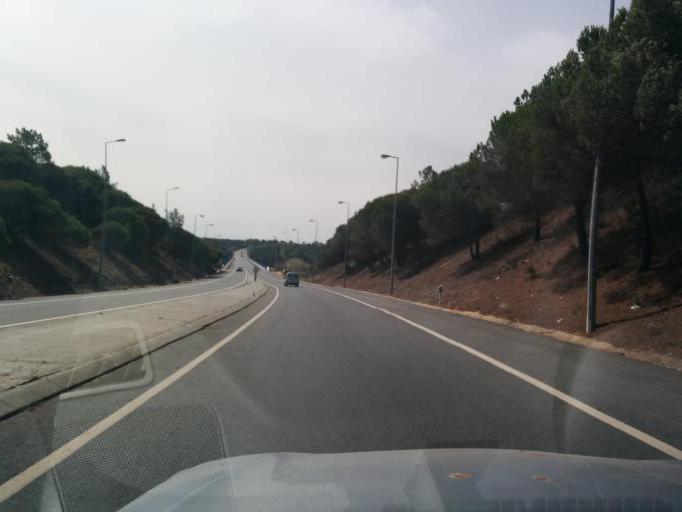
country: PT
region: Beja
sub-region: Odemira
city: Vila Nova de Milfontes
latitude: 37.7302
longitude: -8.7718
